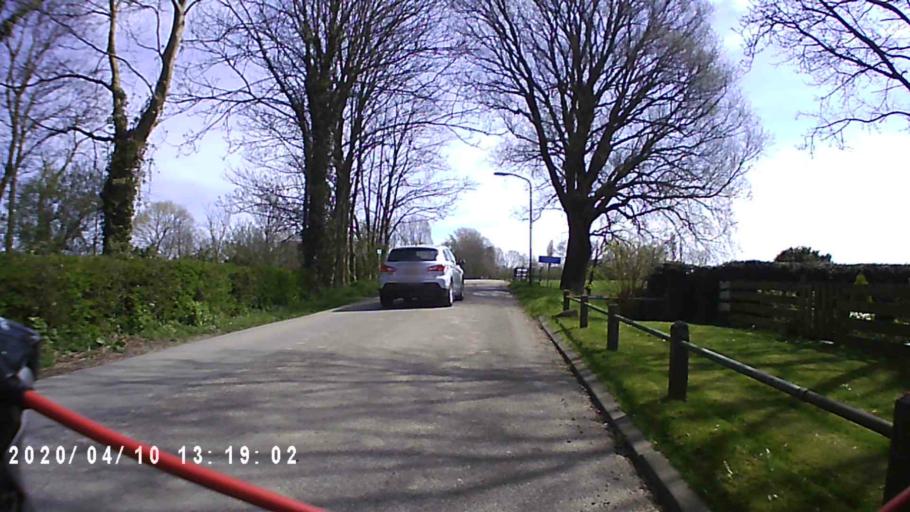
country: NL
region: Groningen
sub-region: Gemeente Zuidhorn
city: Oldehove
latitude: 53.3935
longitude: 6.4256
